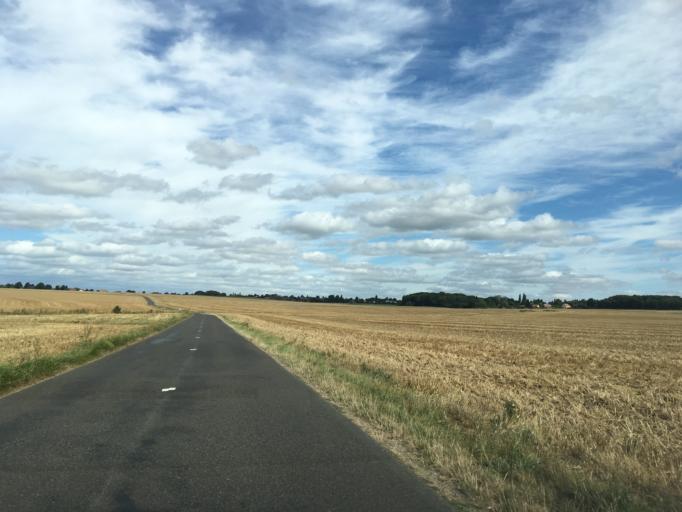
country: FR
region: Haute-Normandie
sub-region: Departement de l'Eure
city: Heudreville-sur-Eure
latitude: 49.1423
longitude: 1.2375
